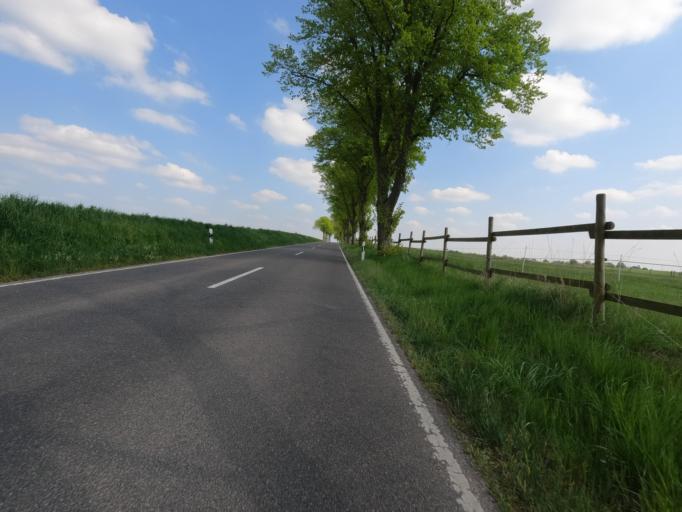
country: DE
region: North Rhine-Westphalia
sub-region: Regierungsbezirk Koln
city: Waldfeucht
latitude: 51.0437
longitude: 6.0412
